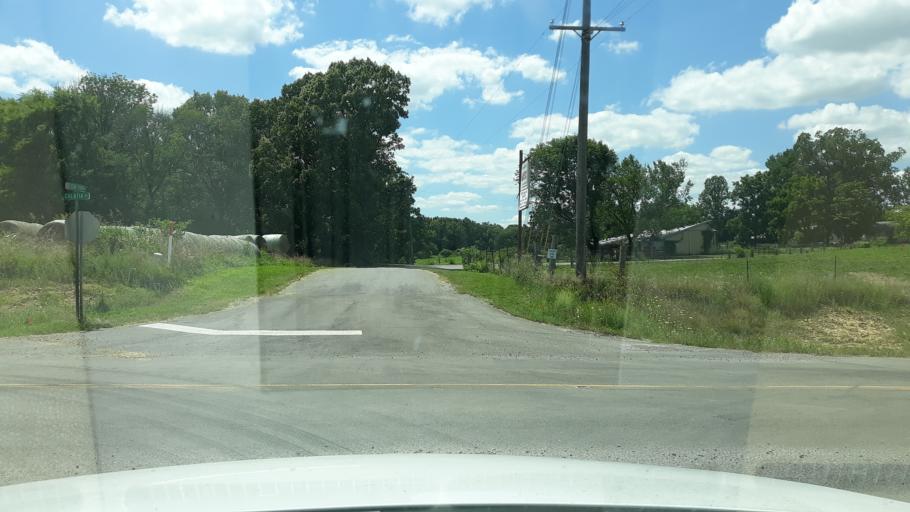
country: US
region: Illinois
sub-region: Saline County
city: Harrisburg
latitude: 37.8633
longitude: -88.6055
